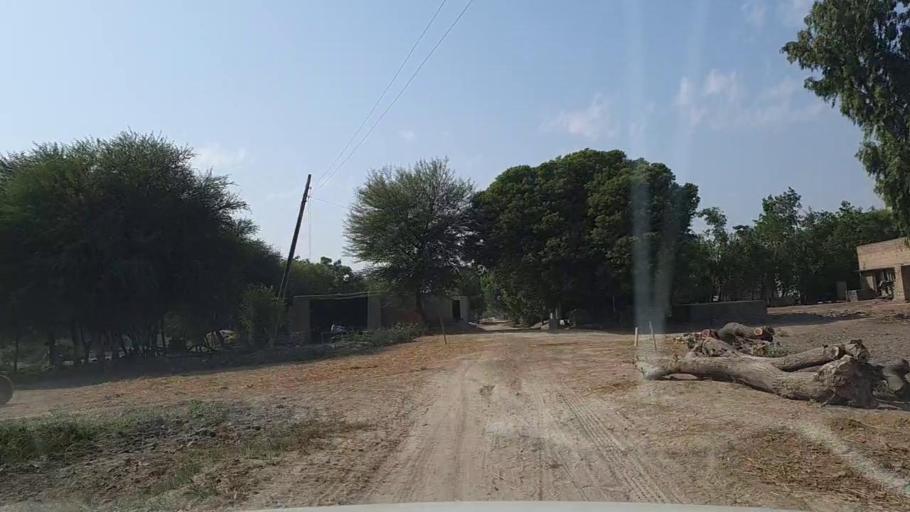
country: PK
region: Sindh
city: Mirpur Batoro
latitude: 24.6759
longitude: 68.3726
